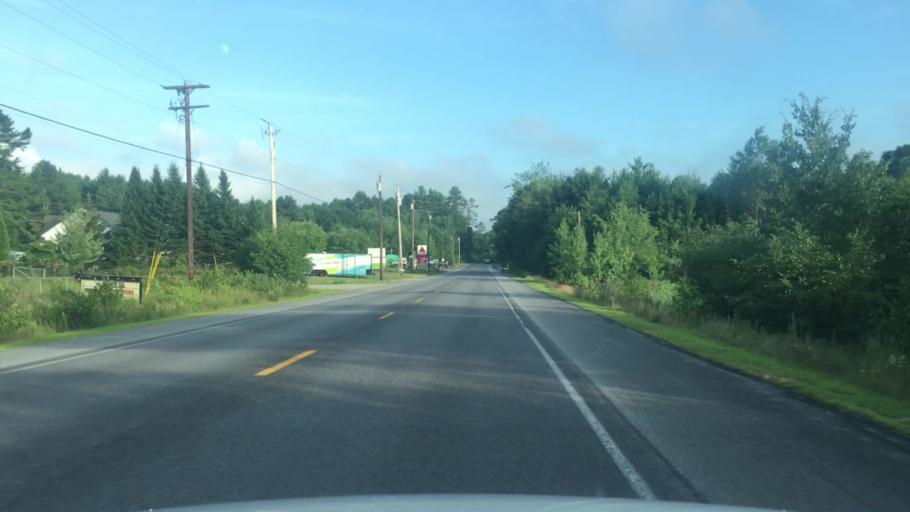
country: US
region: Maine
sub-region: Cumberland County
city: North Windham
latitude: 43.7969
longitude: -70.4011
